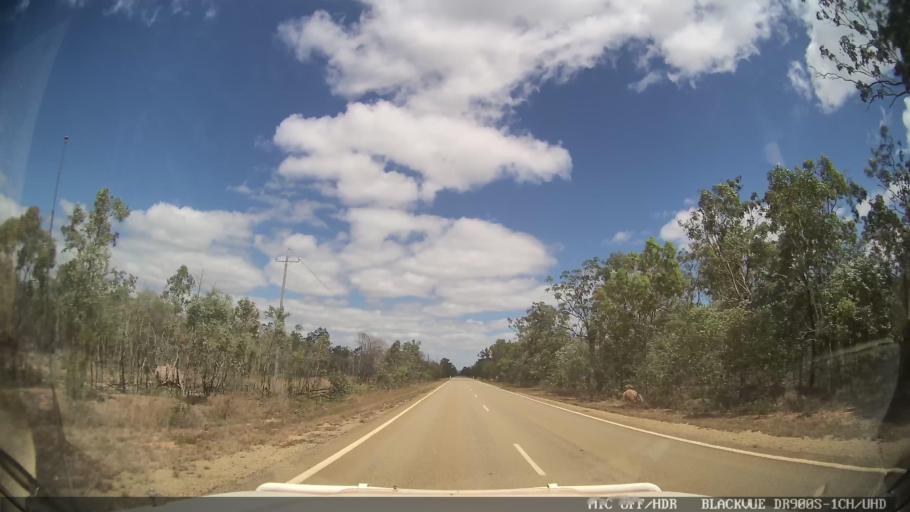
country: AU
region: Queensland
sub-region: Tablelands
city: Ravenshoe
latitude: -17.8137
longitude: 144.9569
